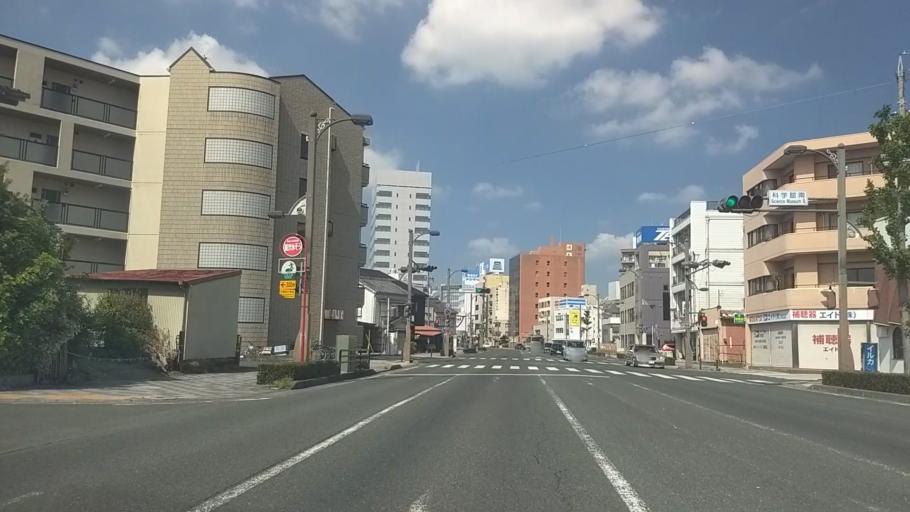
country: JP
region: Shizuoka
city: Hamamatsu
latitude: 34.7033
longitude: 137.7401
